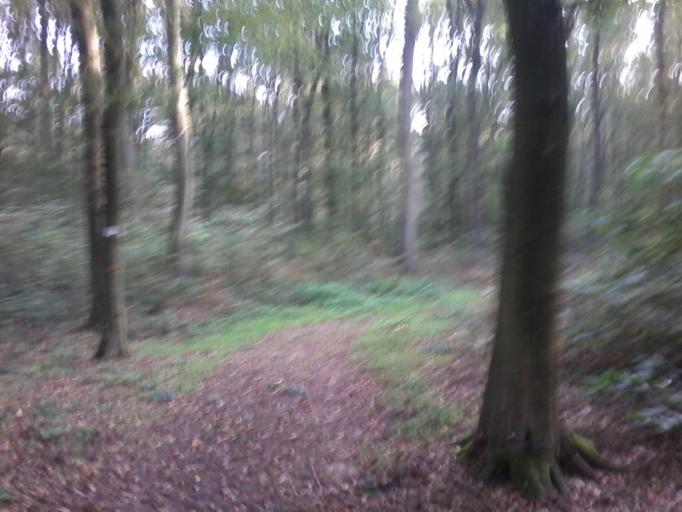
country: HU
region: Vas
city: Sarvar
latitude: 47.1589
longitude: 17.0308
